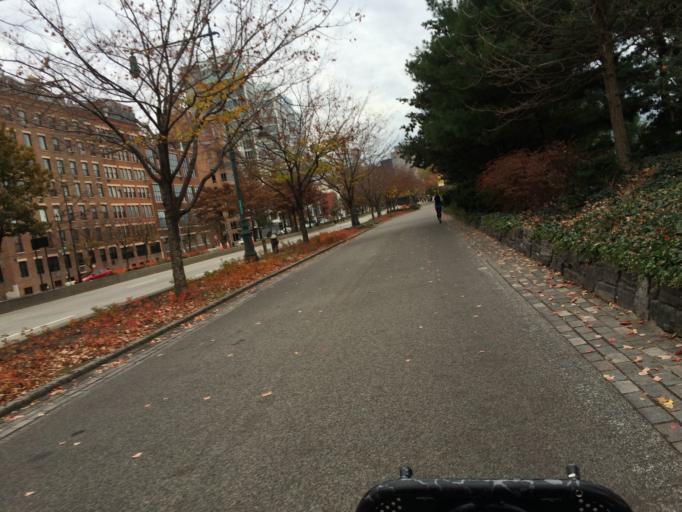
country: US
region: New York
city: New York City
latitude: 40.7365
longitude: -74.0102
